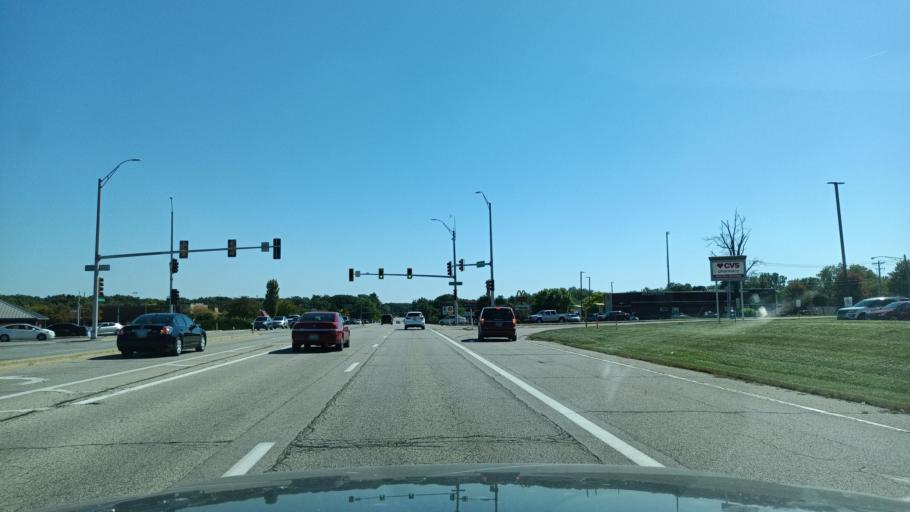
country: US
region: Illinois
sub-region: Peoria County
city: West Peoria
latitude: 40.7714
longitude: -89.6577
